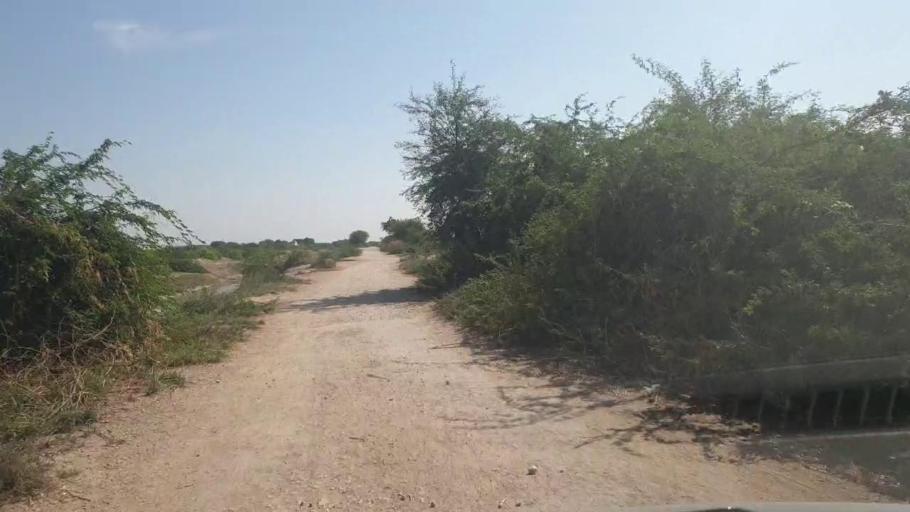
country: PK
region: Sindh
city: Digri
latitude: 24.9467
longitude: 69.1544
